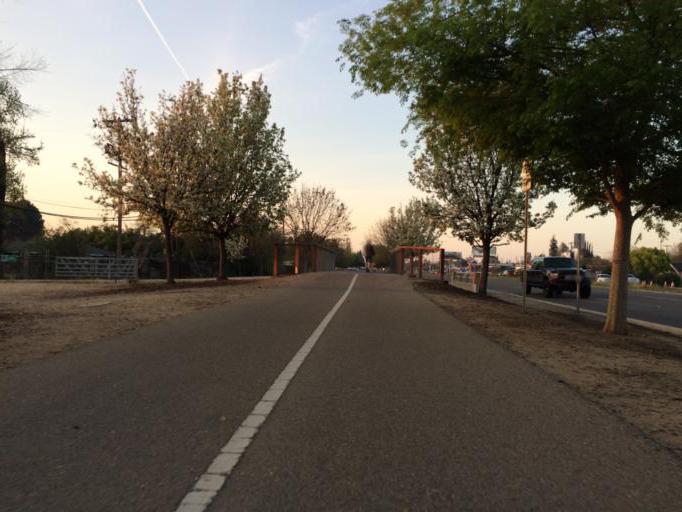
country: US
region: California
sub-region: Fresno County
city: Tarpey Village
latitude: 36.7953
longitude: -119.7004
